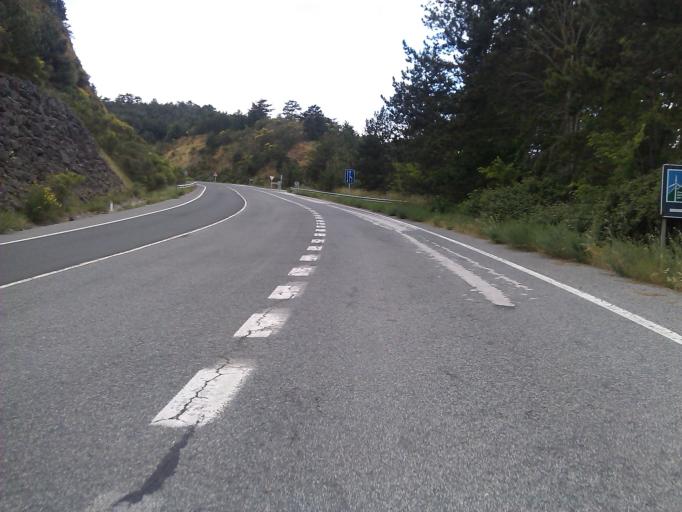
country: ES
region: Navarre
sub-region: Provincia de Navarra
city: Legarda
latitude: 42.7424
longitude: -1.7637
